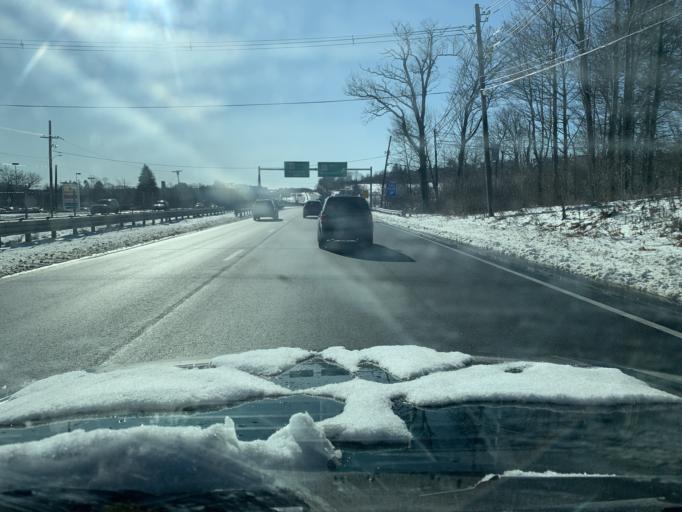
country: US
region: Massachusetts
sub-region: Essex County
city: Danvers
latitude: 42.5870
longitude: -70.9661
